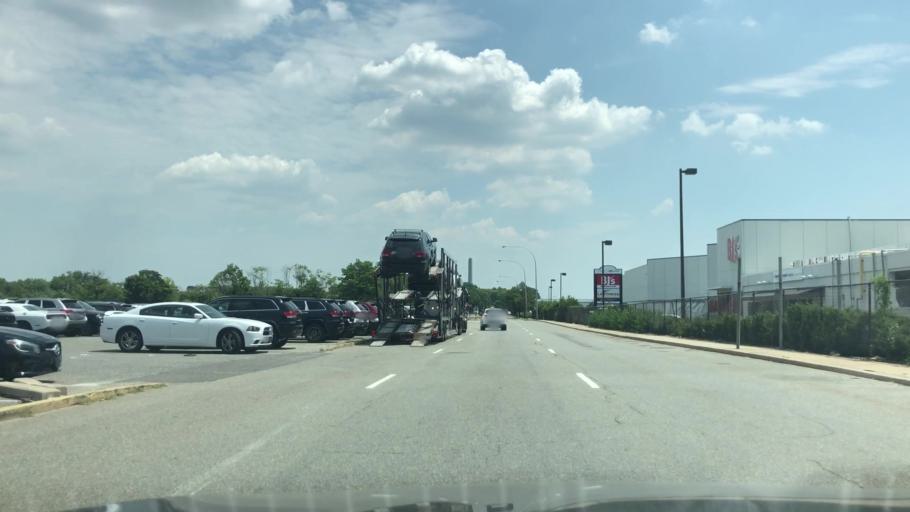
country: US
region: New York
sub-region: Nassau County
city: East Garden City
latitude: 40.7340
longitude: -73.6104
